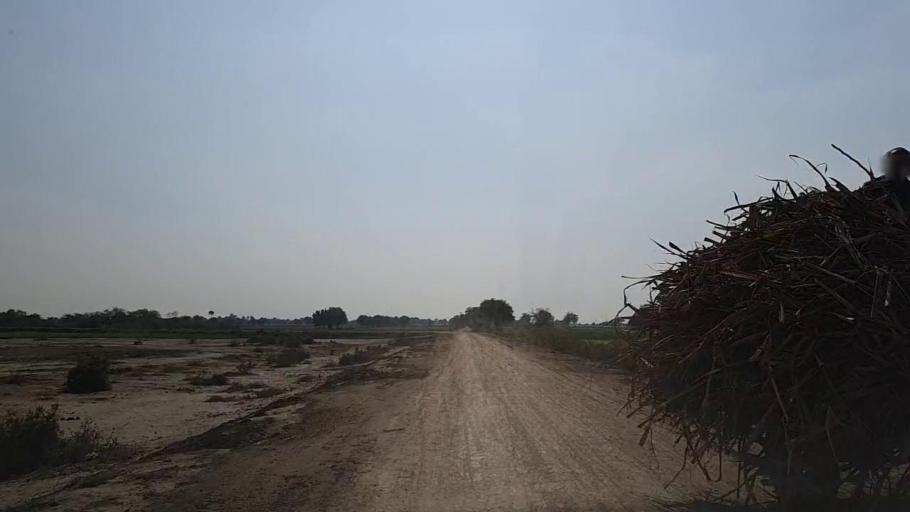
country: PK
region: Sindh
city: Nawabshah
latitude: 26.2583
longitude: 68.4900
